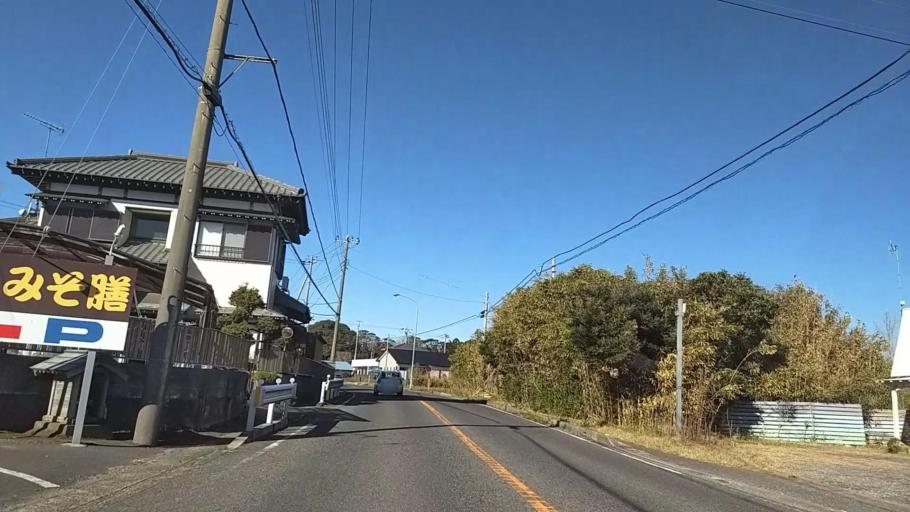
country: JP
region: Chiba
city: Ohara
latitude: 35.3221
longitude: 140.4026
